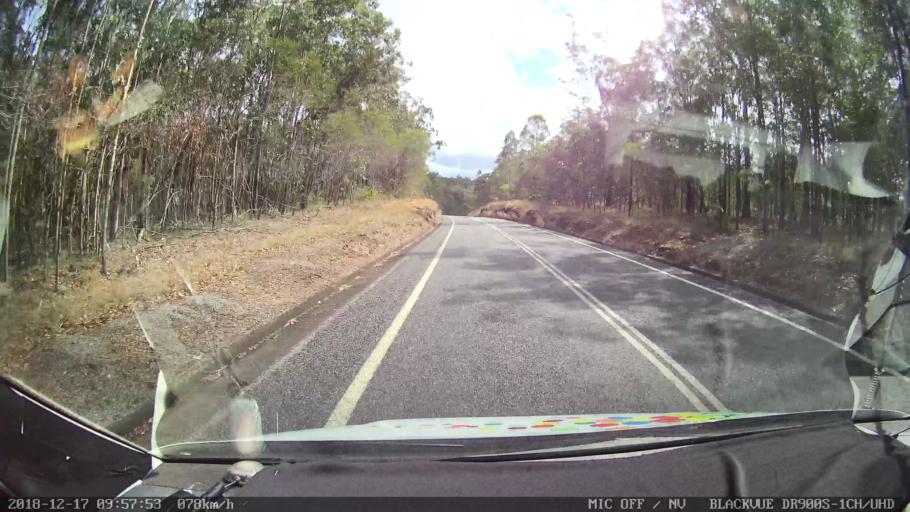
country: AU
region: New South Wales
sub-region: Tenterfield Municipality
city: Carrolls Creek
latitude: -28.9232
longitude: 152.4028
